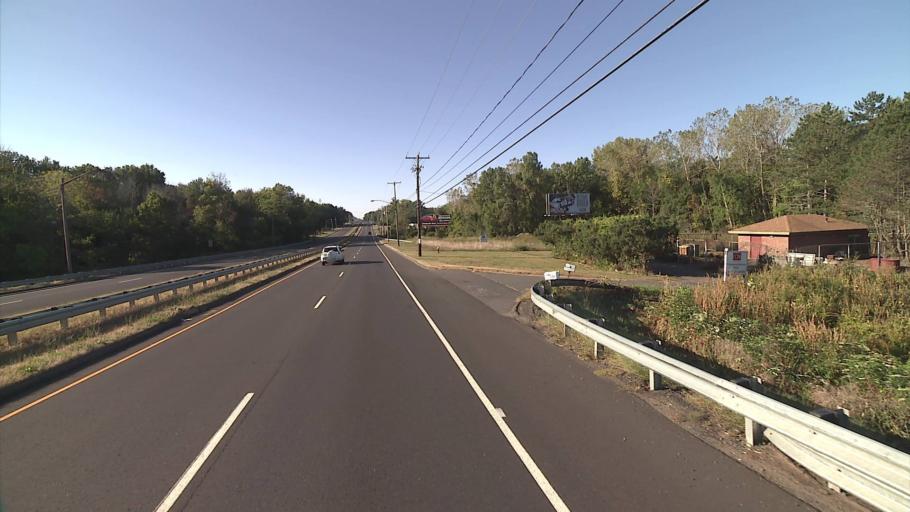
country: US
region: Connecticut
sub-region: Hartford County
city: Kensington
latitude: 41.6384
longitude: -72.7350
